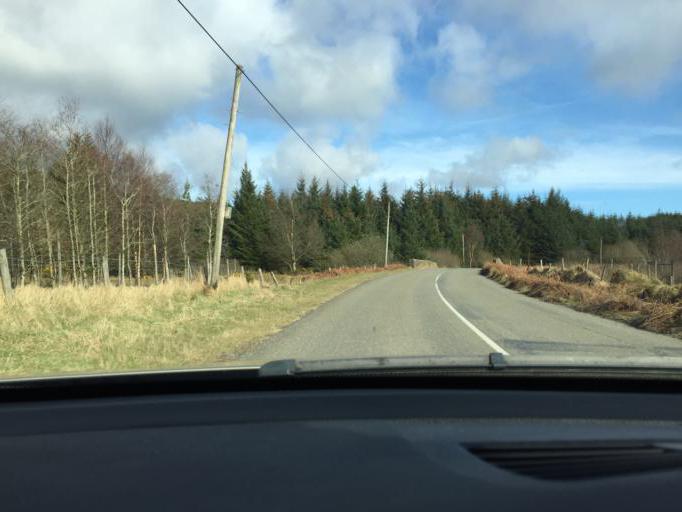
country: IE
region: Leinster
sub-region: Wicklow
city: Valleymount
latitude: 53.0624
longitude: -6.4560
